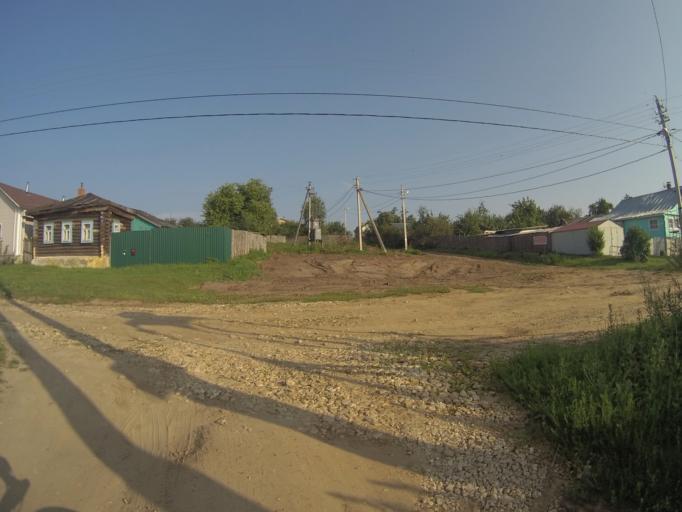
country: RU
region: Vladimir
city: Kommunar
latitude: 56.1188
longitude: 40.4999
